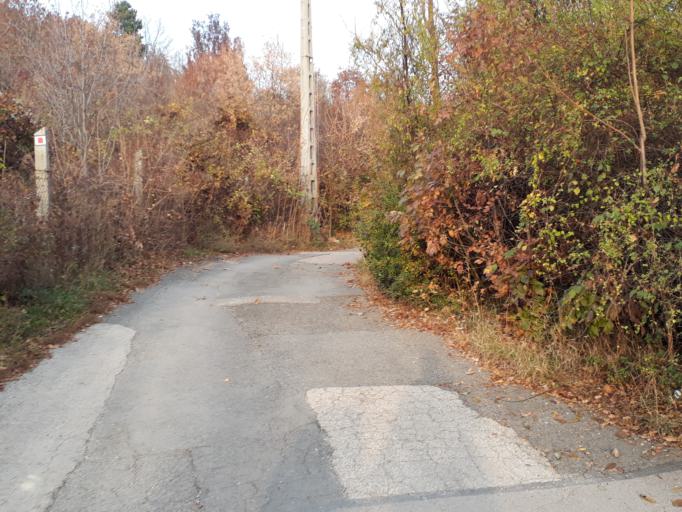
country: HU
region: Pest
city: Budaors
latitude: 47.4767
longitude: 18.9749
